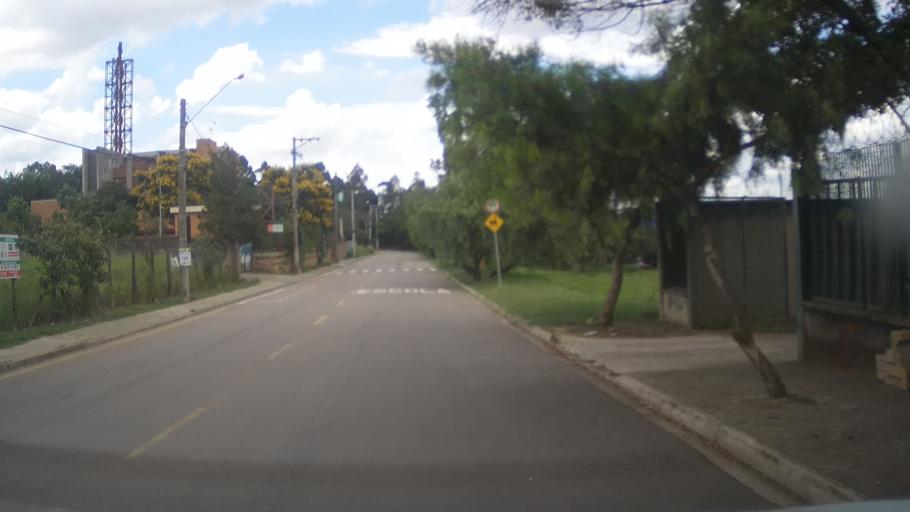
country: BR
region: Sao Paulo
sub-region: Itupeva
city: Itupeva
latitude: -23.1777
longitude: -46.9894
